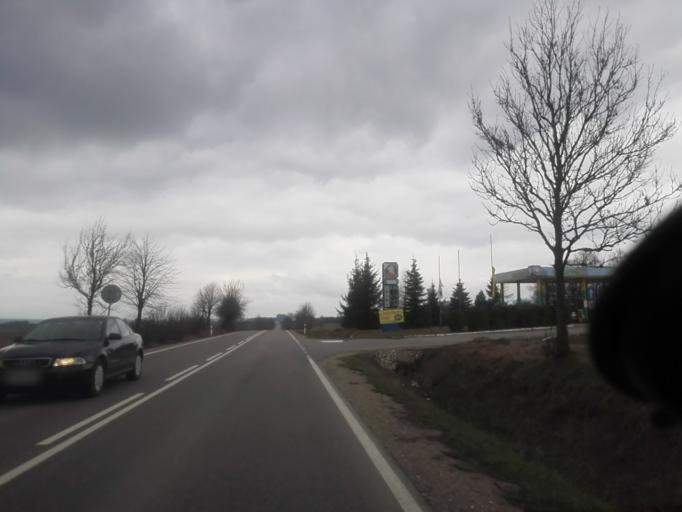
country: PL
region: Podlasie
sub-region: Suwalki
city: Suwalki
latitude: 54.2156
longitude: 22.9122
